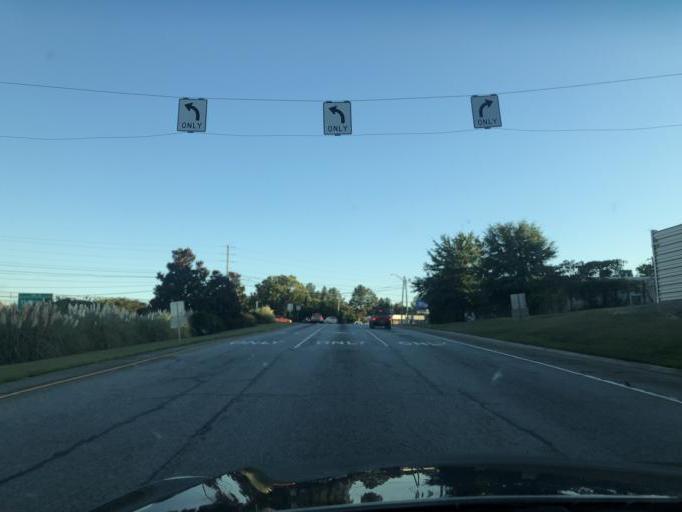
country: US
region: Georgia
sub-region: Muscogee County
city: Columbus
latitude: 32.4632
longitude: -84.9296
